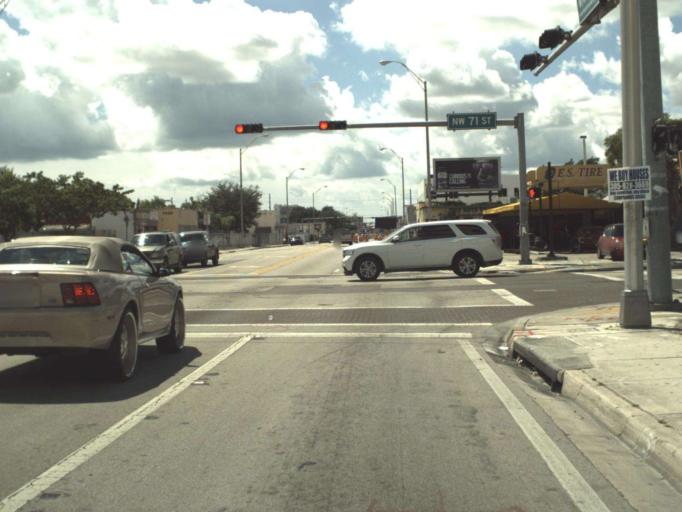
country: US
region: Florida
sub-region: Miami-Dade County
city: El Portal
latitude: 25.8399
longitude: -80.2089
